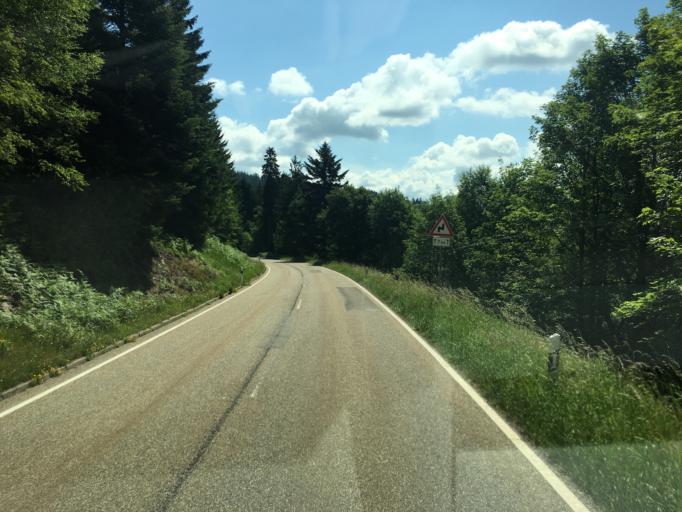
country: DE
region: Baden-Wuerttemberg
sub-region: Freiburg Region
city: Seebach
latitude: 48.5599
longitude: 8.2283
